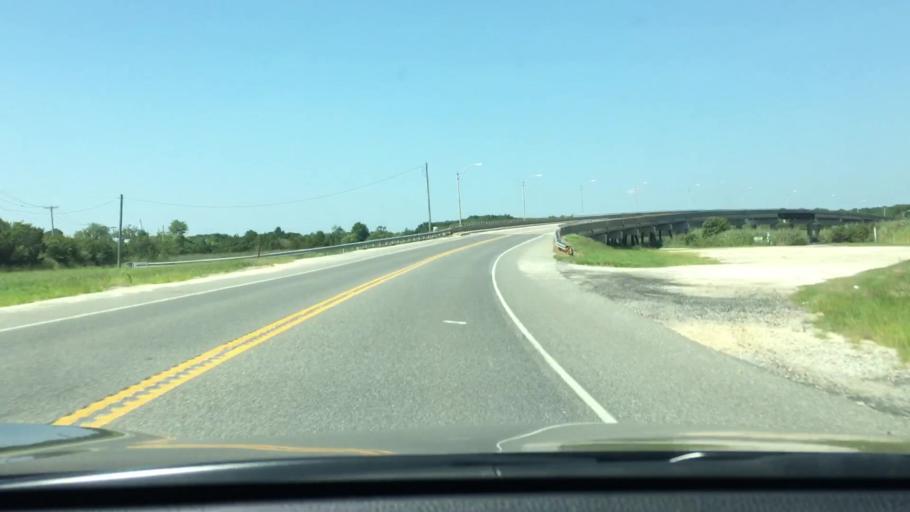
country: US
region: New Jersey
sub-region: Cumberland County
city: Port Norris
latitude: 39.2868
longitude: -74.9861
